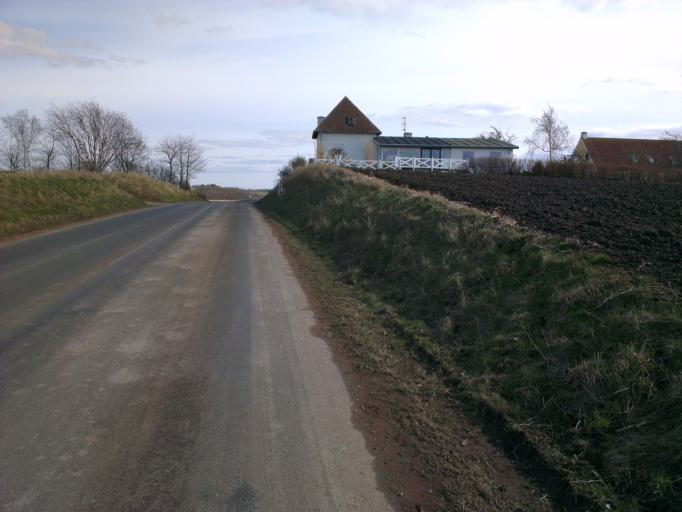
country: DK
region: Capital Region
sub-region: Frederikssund Kommune
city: Skibby
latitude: 55.7485
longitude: 11.9846
